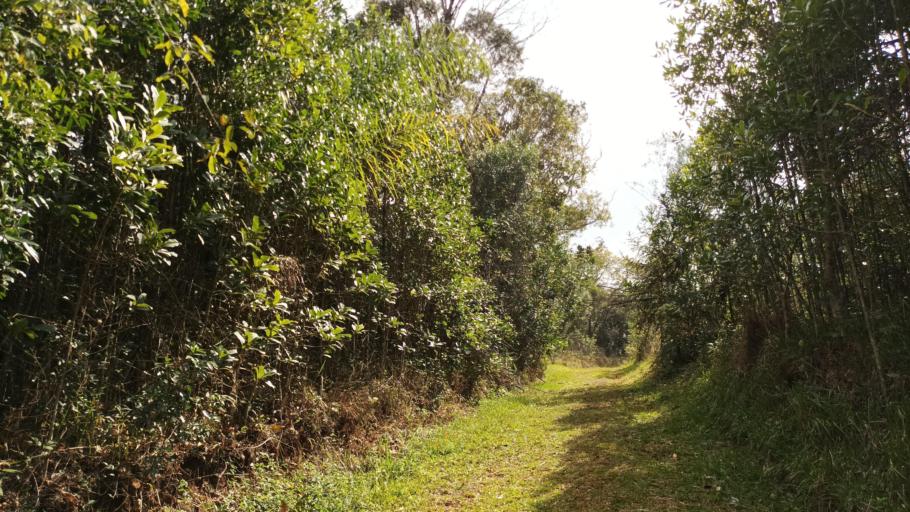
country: AR
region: Misiones
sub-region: Departamento de San Pedro
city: San Pedro
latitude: -26.6307
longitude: -54.1045
